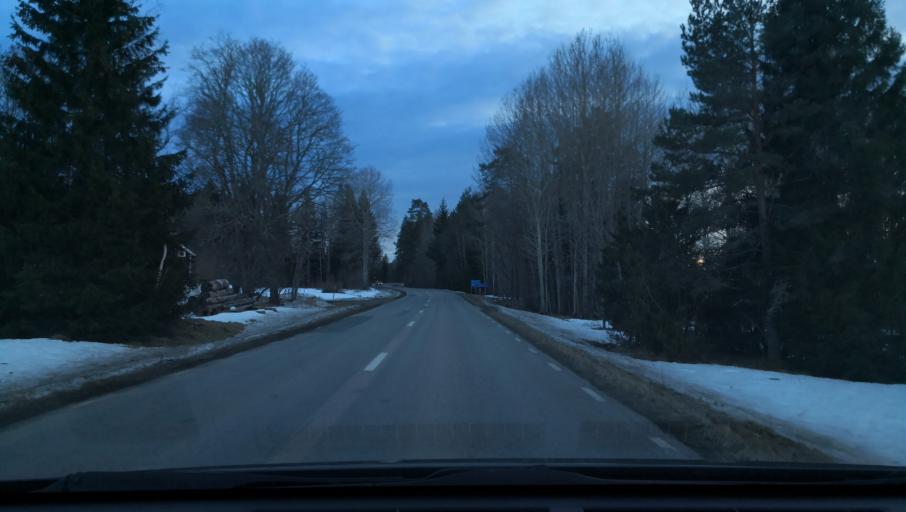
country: SE
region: Uppsala
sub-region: Osthammars Kommun
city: Osterbybruk
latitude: 60.2630
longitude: 17.9529
